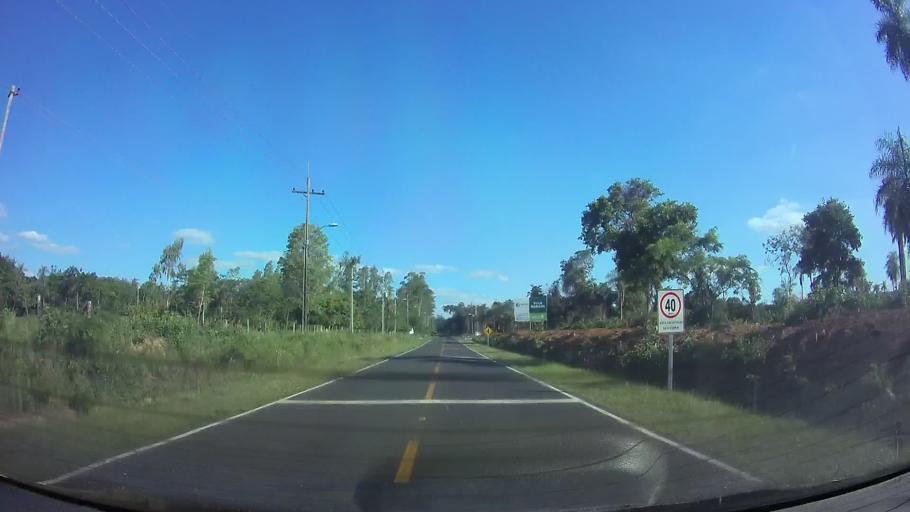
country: PY
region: Cordillera
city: Atyra
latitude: -25.3004
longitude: -57.1608
